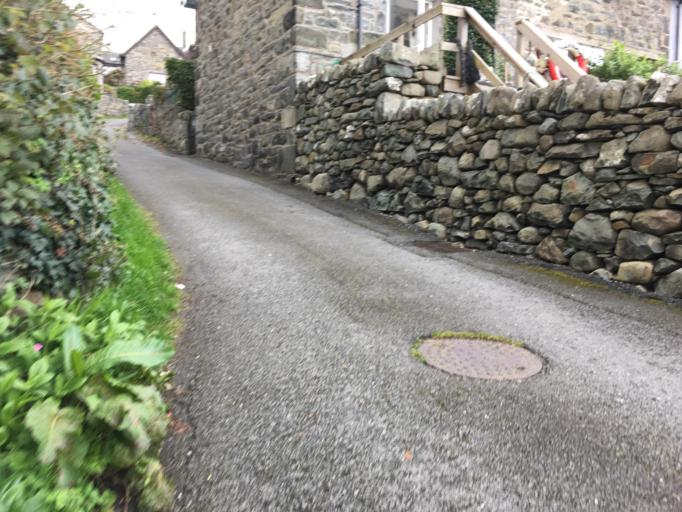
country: GB
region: Wales
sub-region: Gwynedd
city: Llanfair
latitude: 52.8605
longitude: -4.1073
